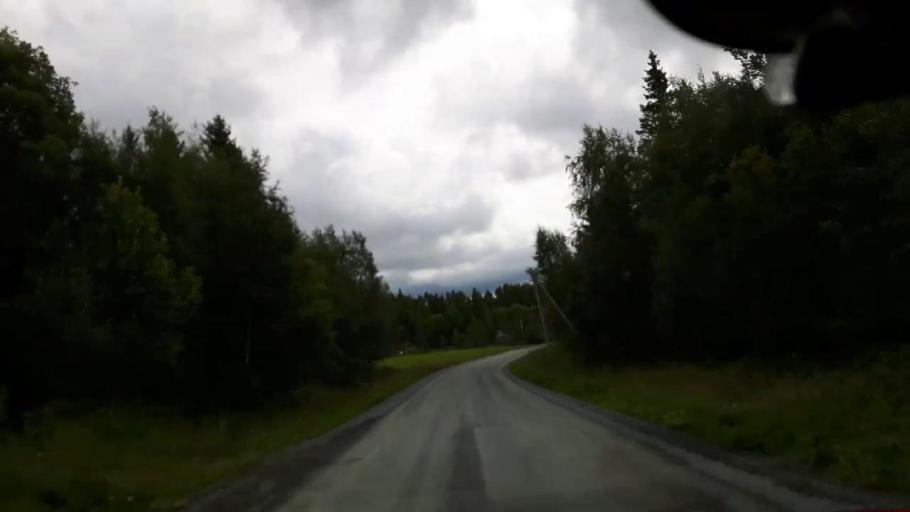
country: SE
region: Jaemtland
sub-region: Krokoms Kommun
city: Krokom
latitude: 63.5732
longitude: 14.2394
